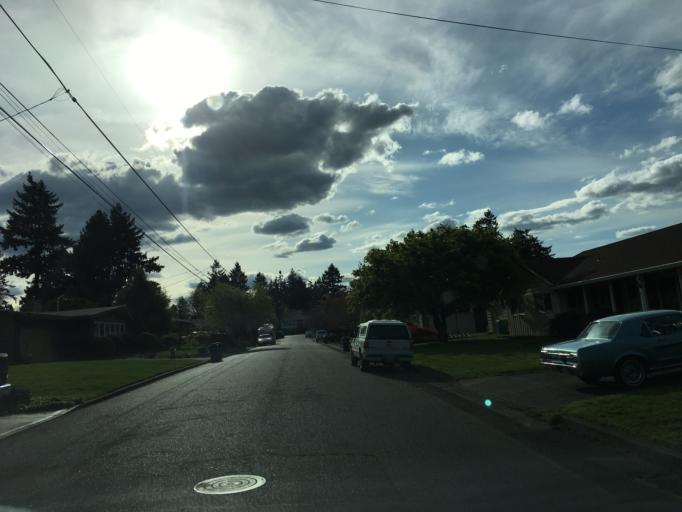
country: US
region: Oregon
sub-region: Multnomah County
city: Lents
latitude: 45.5459
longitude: -122.5399
